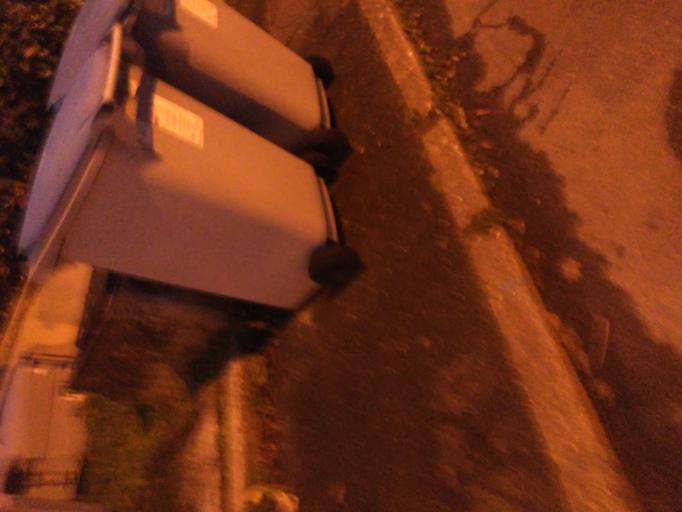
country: FR
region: Pays de la Loire
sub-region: Departement de la Loire-Atlantique
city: Saint-Sebastien-sur-Loire
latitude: 47.1909
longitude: -1.5047
